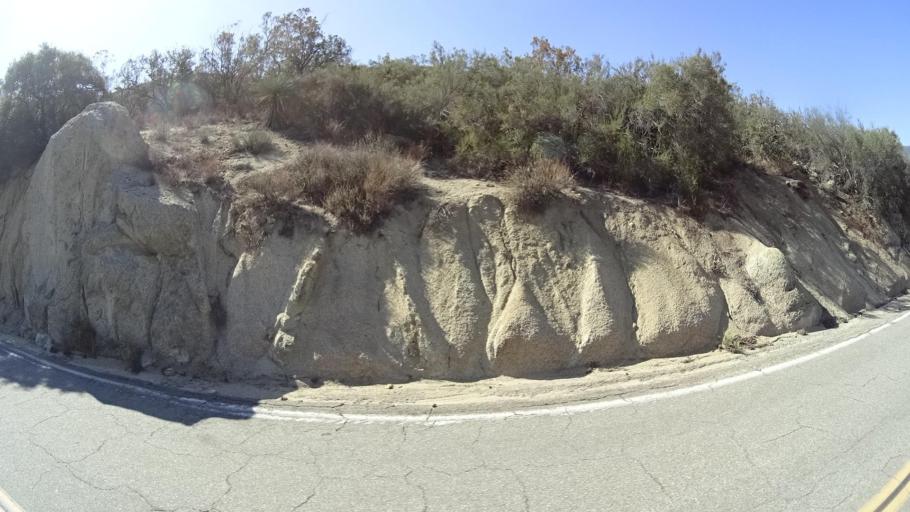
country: US
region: California
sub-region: Riverside County
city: Aguanga
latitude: 33.3720
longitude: -116.7311
